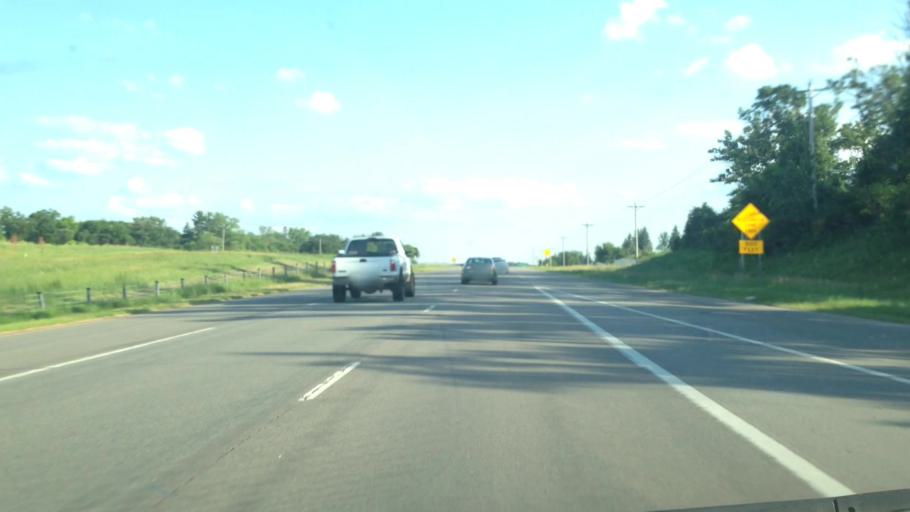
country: US
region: Minnesota
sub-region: Sherburne County
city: Zimmerman
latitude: 45.3779
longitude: -93.5643
